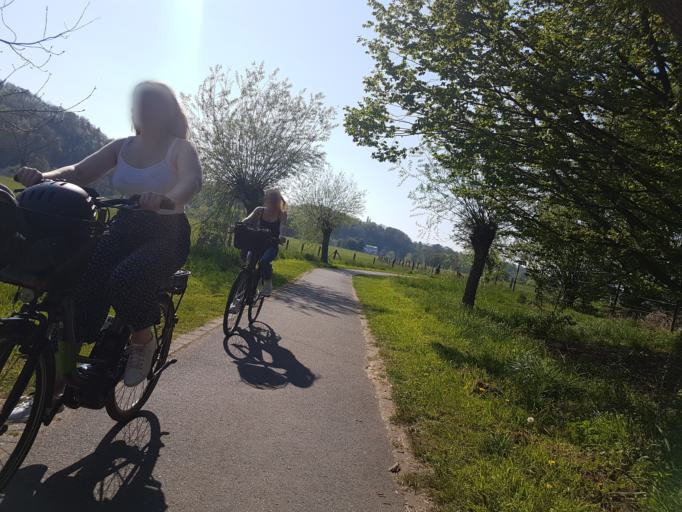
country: DE
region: North Rhine-Westphalia
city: Hattingen
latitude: 51.4138
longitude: 7.2314
